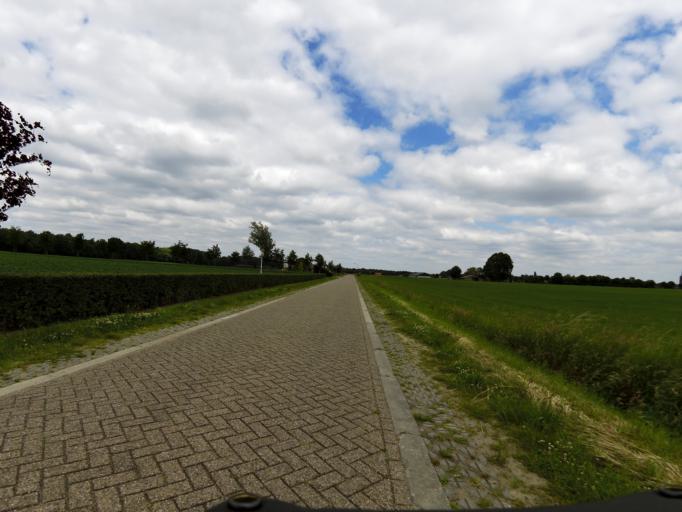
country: NL
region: North Brabant
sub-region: Gemeente Baarle-Nassau
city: Baarle-Nassau
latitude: 51.4785
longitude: 4.9404
